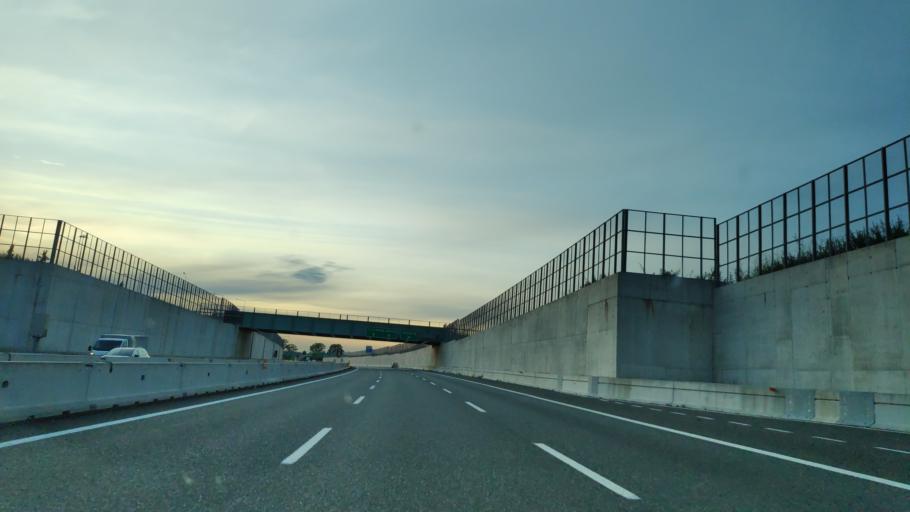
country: IT
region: Lombardy
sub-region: Citta metropolitana di Milano
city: Gessate
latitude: 45.5448
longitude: 9.4272
